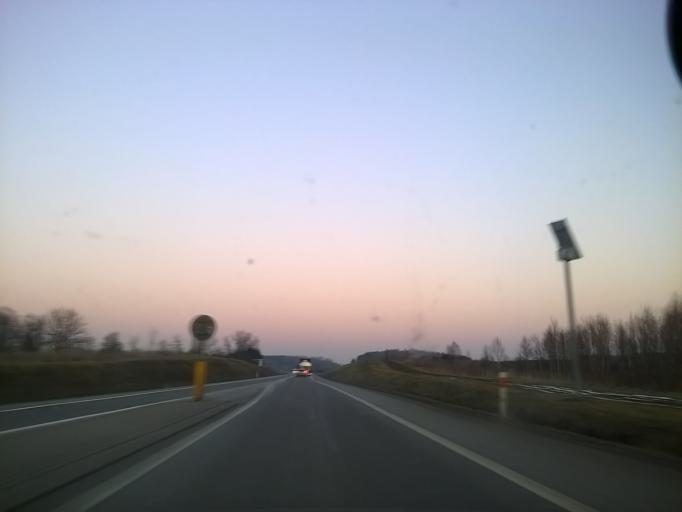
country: PL
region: Warmian-Masurian Voivodeship
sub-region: Powiat olsztynski
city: Olsztyn
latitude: 53.7867
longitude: 20.5932
